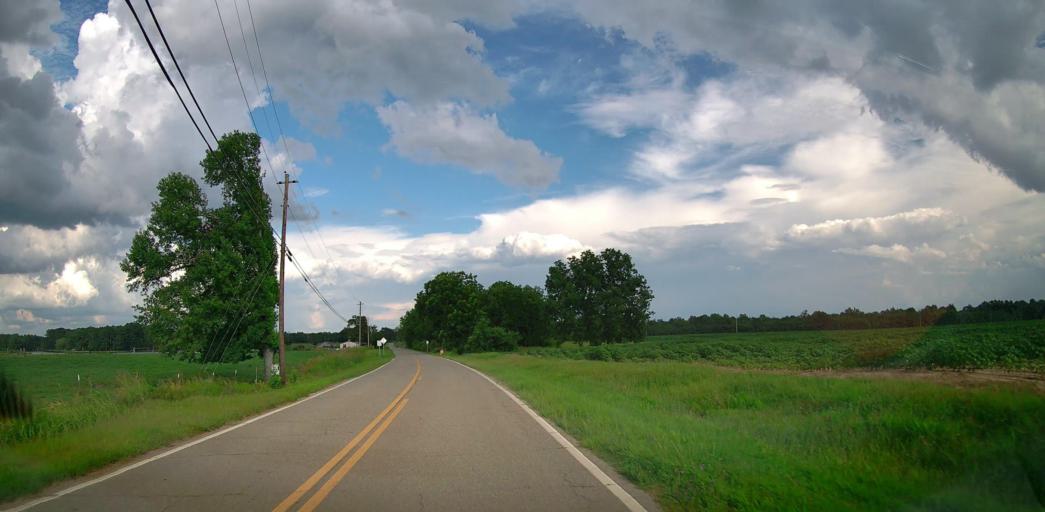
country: US
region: Georgia
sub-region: Bleckley County
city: Cochran
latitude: 32.3973
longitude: -83.3723
